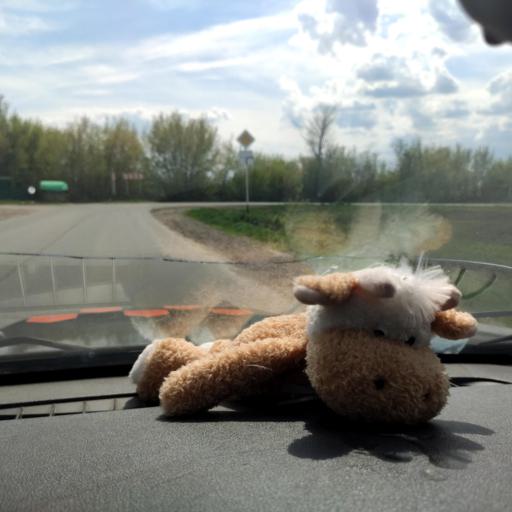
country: RU
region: Samara
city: Podstepki
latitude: 53.5217
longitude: 49.0856
